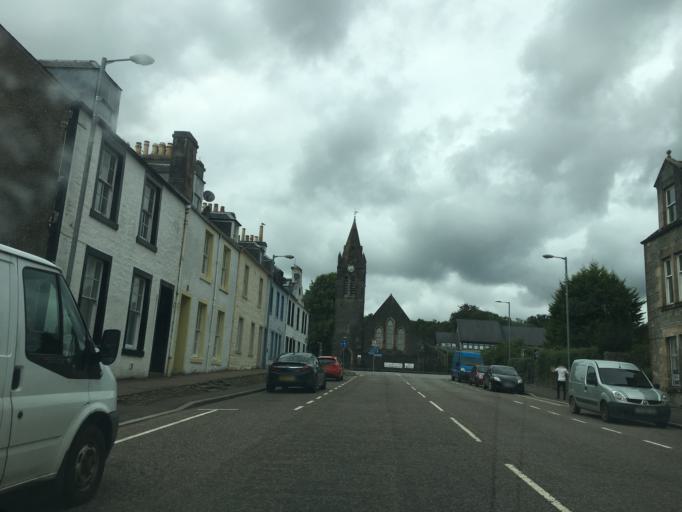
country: GB
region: Scotland
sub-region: Argyll and Bute
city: Lochgilphead
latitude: 56.0384
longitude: -5.4329
